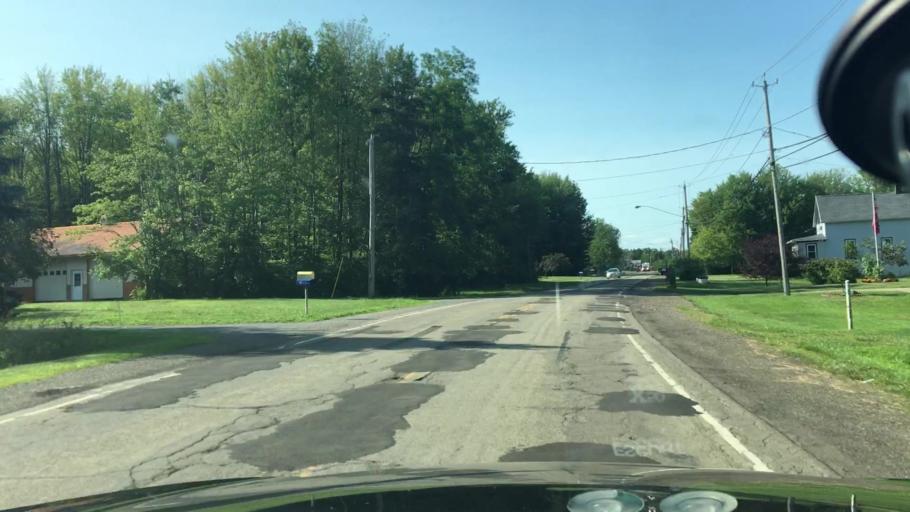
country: US
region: New York
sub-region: Erie County
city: Angola
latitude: 42.6257
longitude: -79.0263
